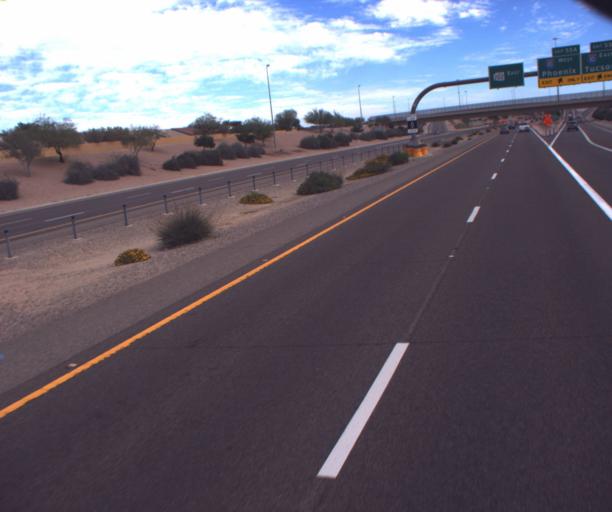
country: US
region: Arizona
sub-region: Maricopa County
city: Guadalupe
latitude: 33.2934
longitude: -111.9831
